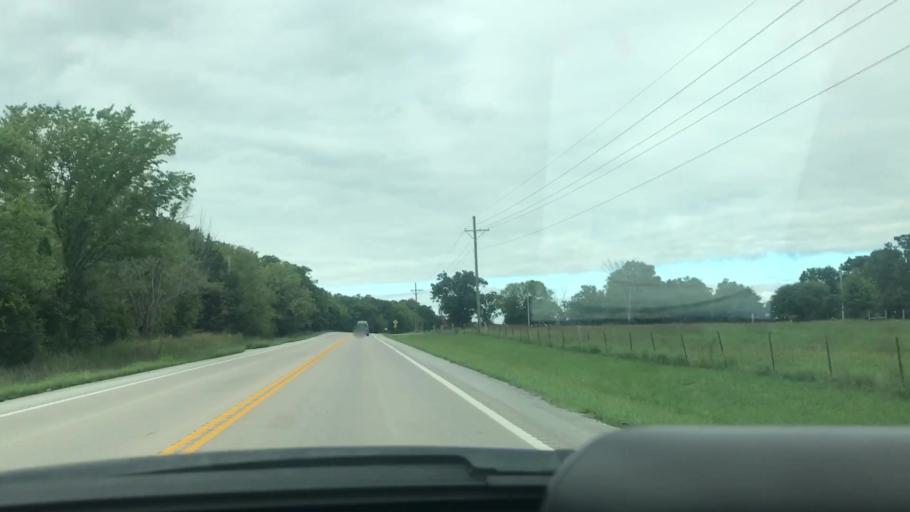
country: US
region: Missouri
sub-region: Hickory County
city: Hermitage
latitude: 37.8688
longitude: -93.1800
